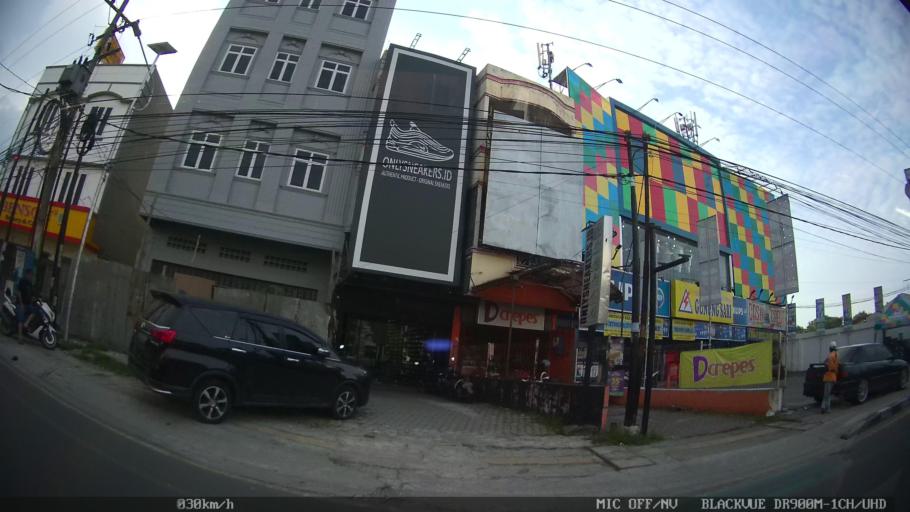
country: ID
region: North Sumatra
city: Sunggal
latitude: 3.5664
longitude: 98.6411
